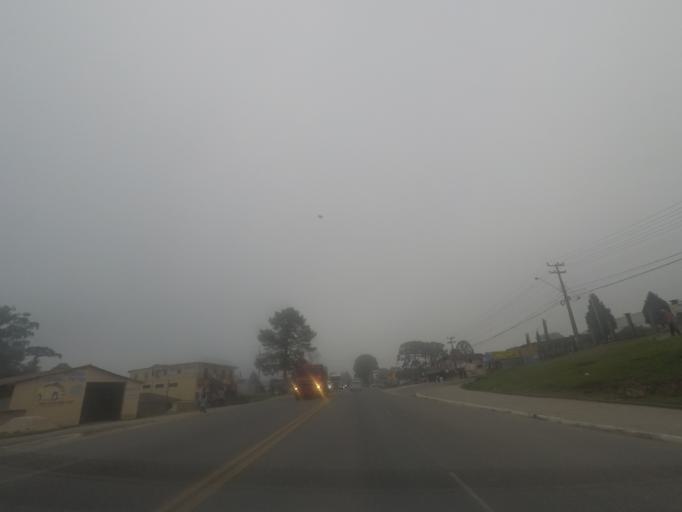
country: BR
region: Parana
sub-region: Itaperucu
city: Itaperucu
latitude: -25.2602
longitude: -49.3026
